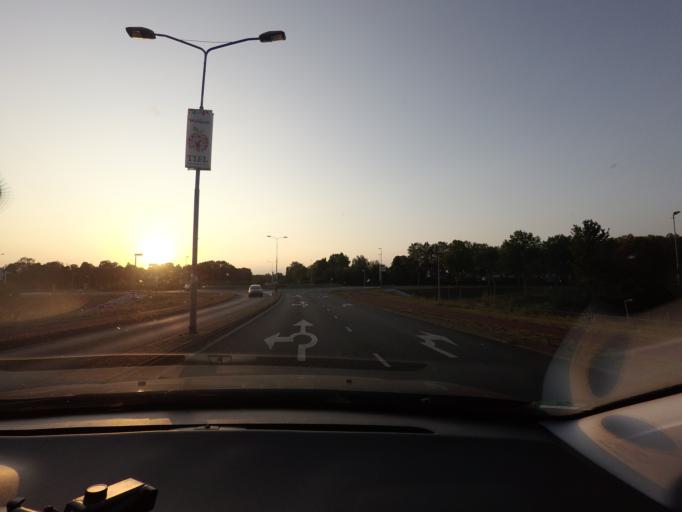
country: NL
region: Gelderland
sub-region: Gemeente Tiel
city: Tiel
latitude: 51.8833
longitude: 5.4054
